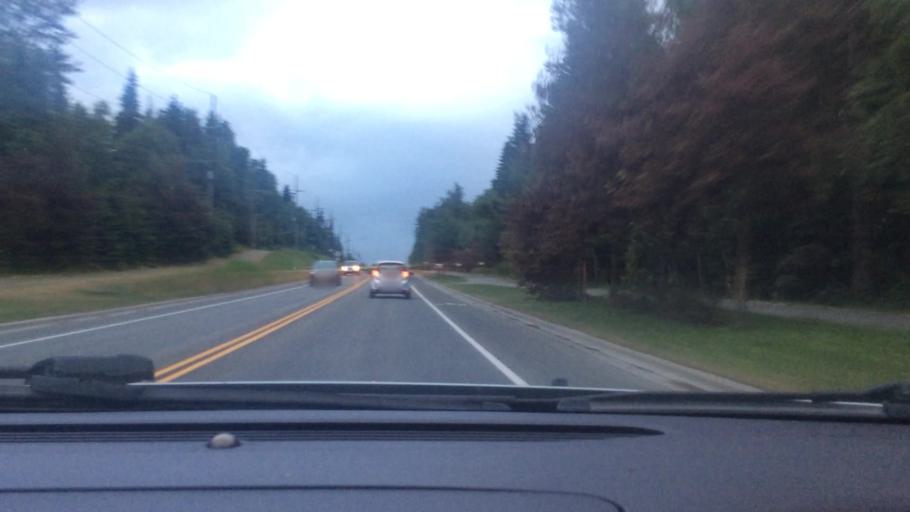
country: US
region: Alaska
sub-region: Anchorage Municipality
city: Anchorage
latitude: 61.1434
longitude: -149.8042
